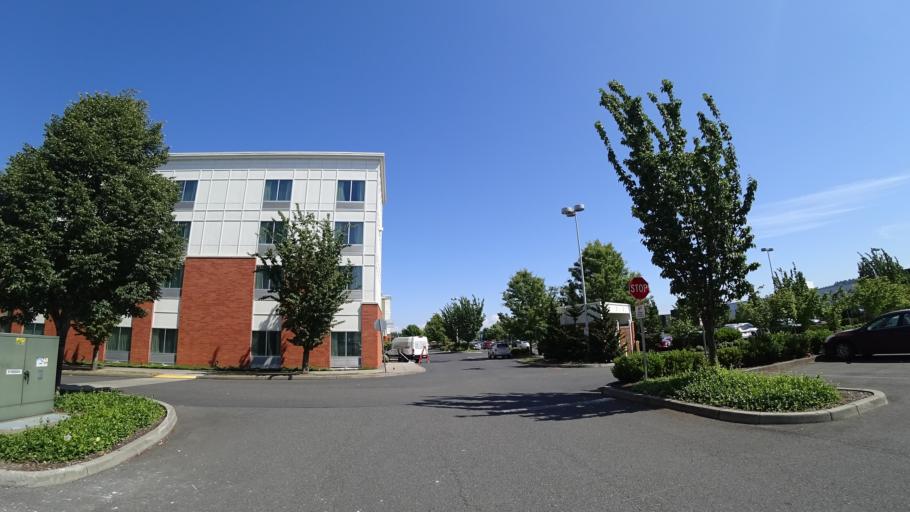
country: US
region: Washington
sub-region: Clark County
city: Orchards
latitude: 45.5741
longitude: -122.5636
